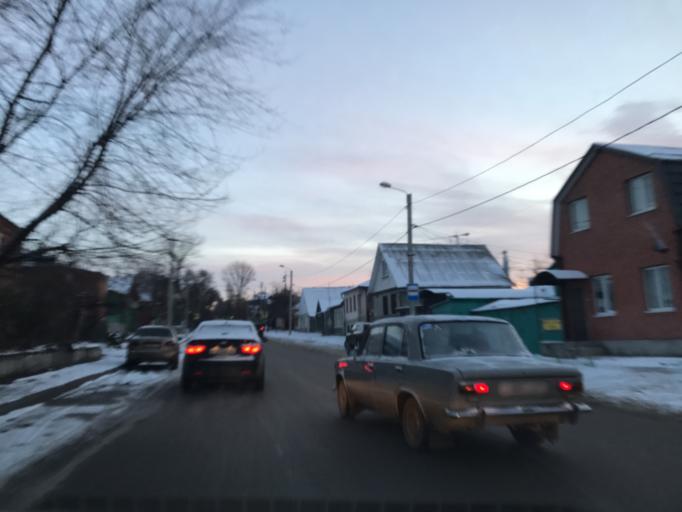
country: RU
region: Rostov
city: Rostov-na-Donu
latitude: 47.2268
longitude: 39.6820
